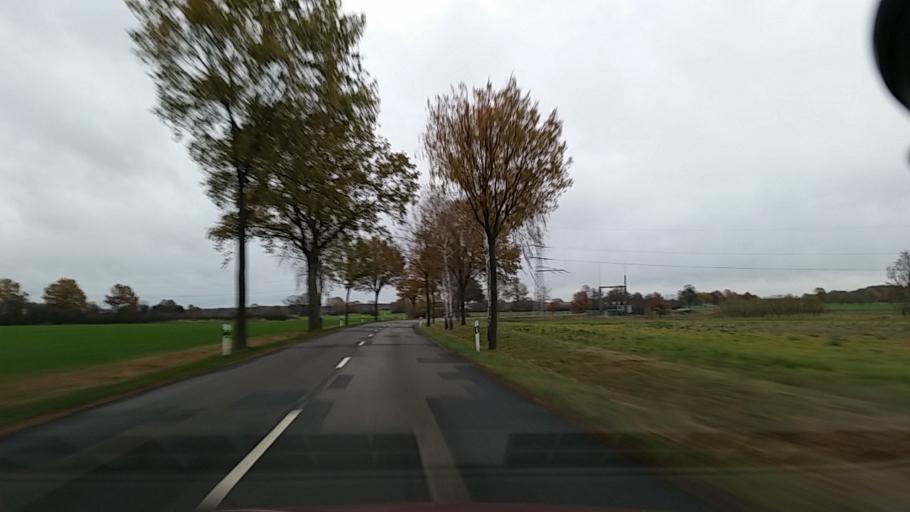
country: DE
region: Lower Saxony
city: Jembke
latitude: 52.5004
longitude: 10.7789
